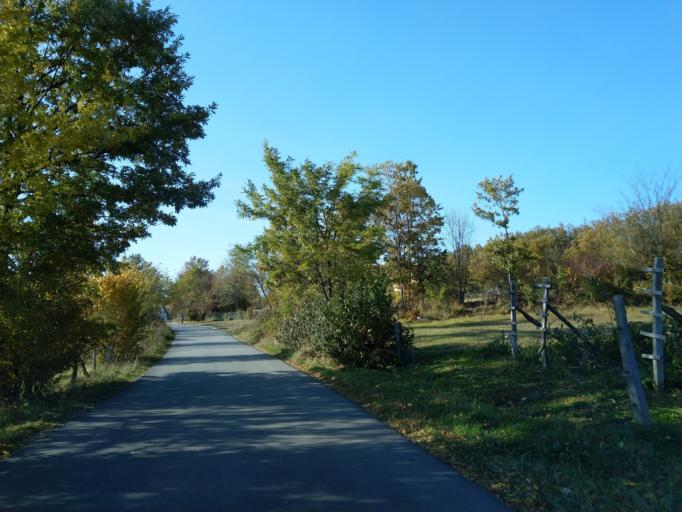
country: RS
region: Central Serbia
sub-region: Zlatiborski Okrug
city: Uzice
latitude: 43.8679
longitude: 19.7612
